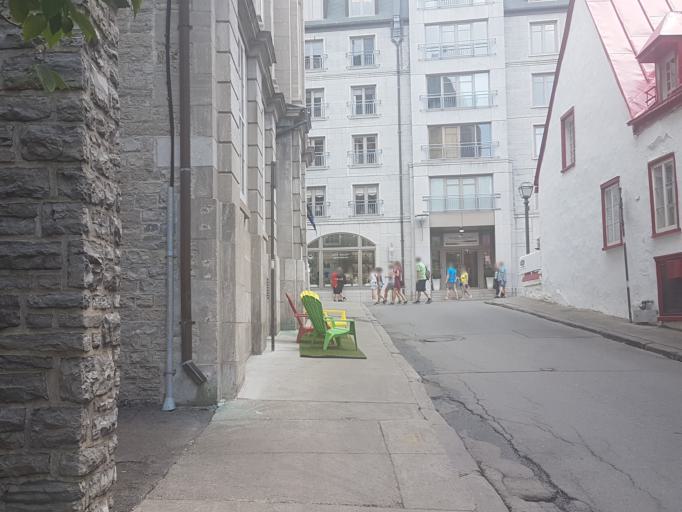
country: CA
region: Quebec
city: Quebec
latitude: 46.8120
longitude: -71.2074
